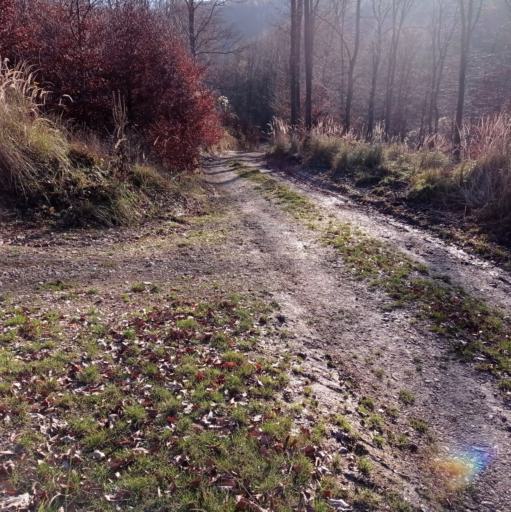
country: HU
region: Veszprem
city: Zirc
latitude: 47.2172
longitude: 17.9278
